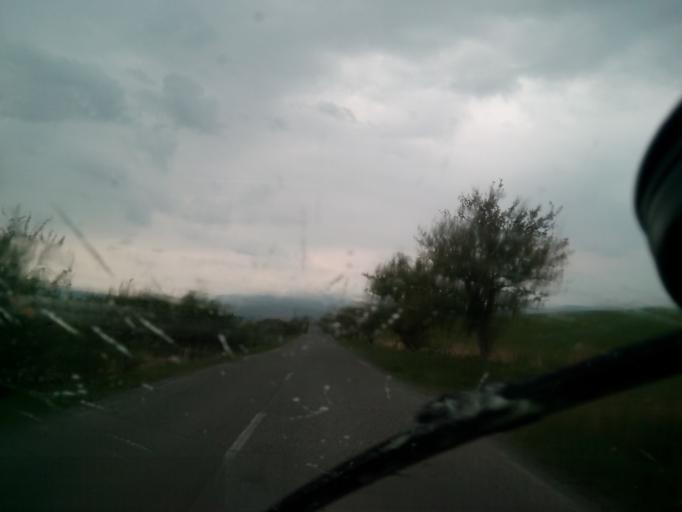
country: SK
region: Kosicky
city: Secovce
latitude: 48.7883
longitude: 21.4798
